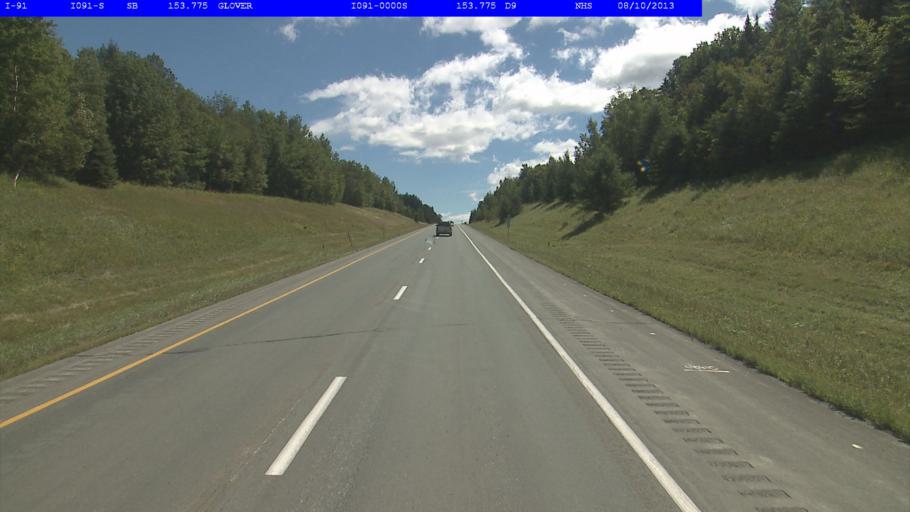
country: US
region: Vermont
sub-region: Orleans County
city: Newport
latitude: 44.7091
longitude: -72.1655
